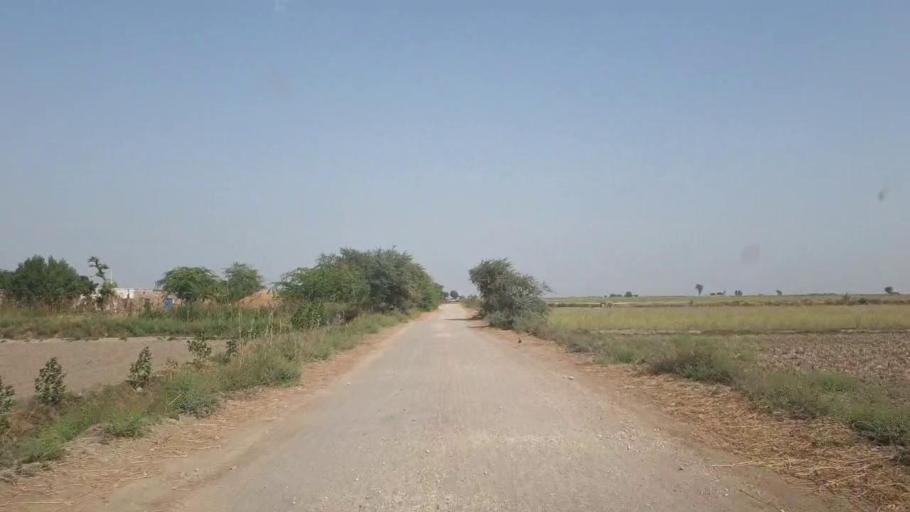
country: PK
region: Sindh
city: Kario
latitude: 24.5357
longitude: 68.5348
